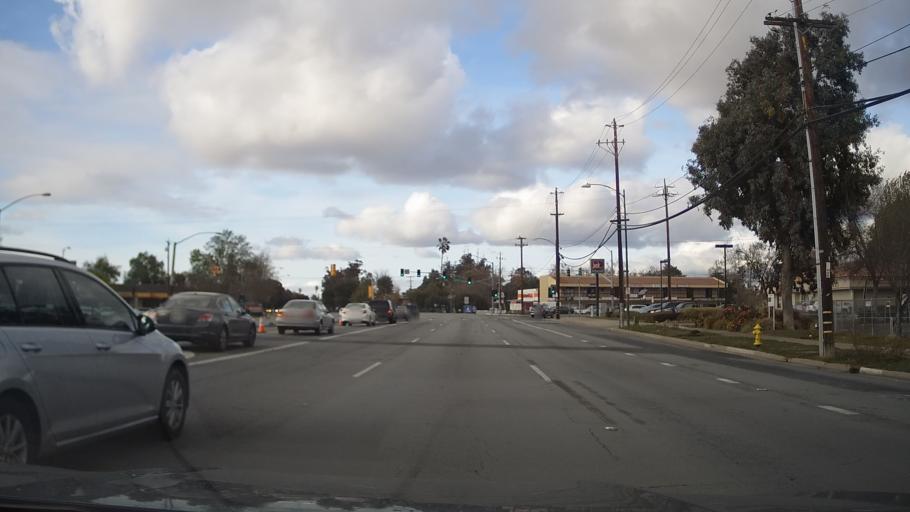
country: US
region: California
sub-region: Santa Clara County
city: Seven Trees
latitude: 37.2619
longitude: -121.8765
